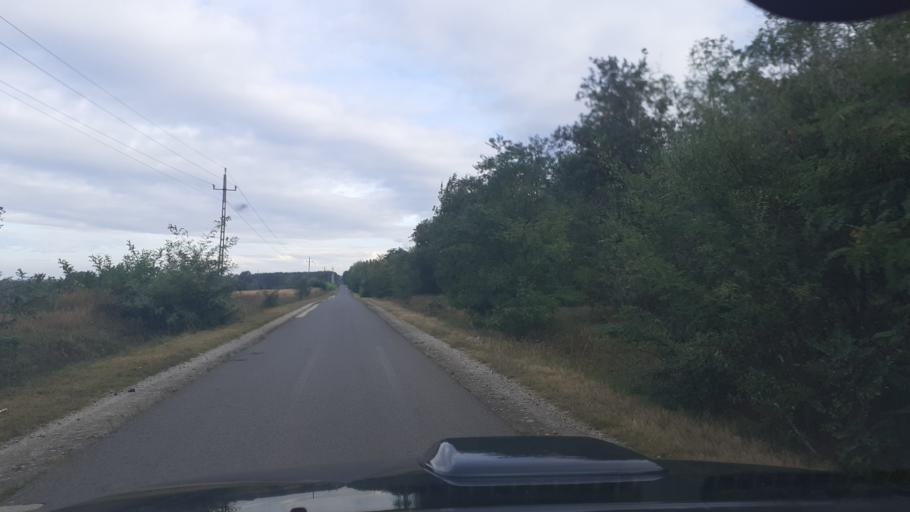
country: HU
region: Fejer
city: Baracs
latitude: 46.9314
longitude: 18.8722
